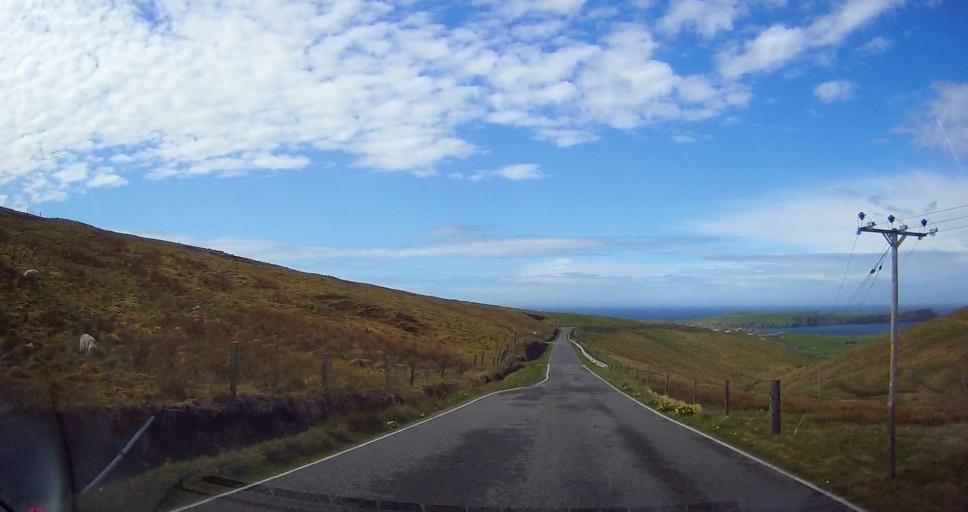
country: GB
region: Scotland
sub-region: Shetland Islands
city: Sandwick
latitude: 59.9793
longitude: -1.2962
